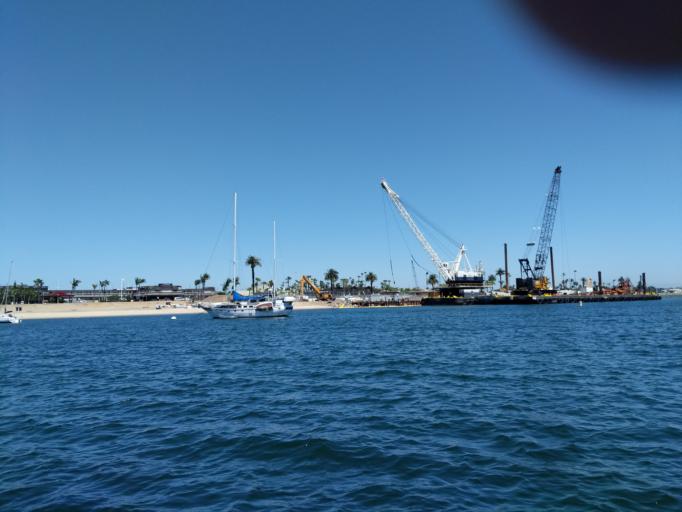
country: US
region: California
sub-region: San Diego County
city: Coronado
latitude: 32.7133
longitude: -117.2236
